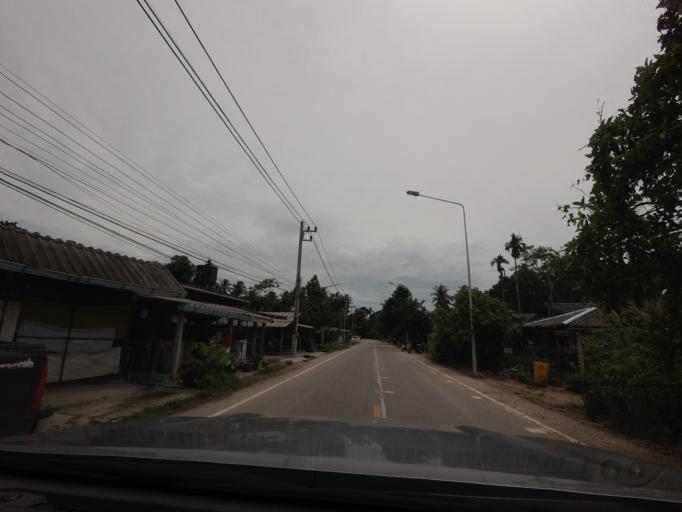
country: TH
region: Pattani
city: Kapho
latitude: 6.5861
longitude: 101.5342
